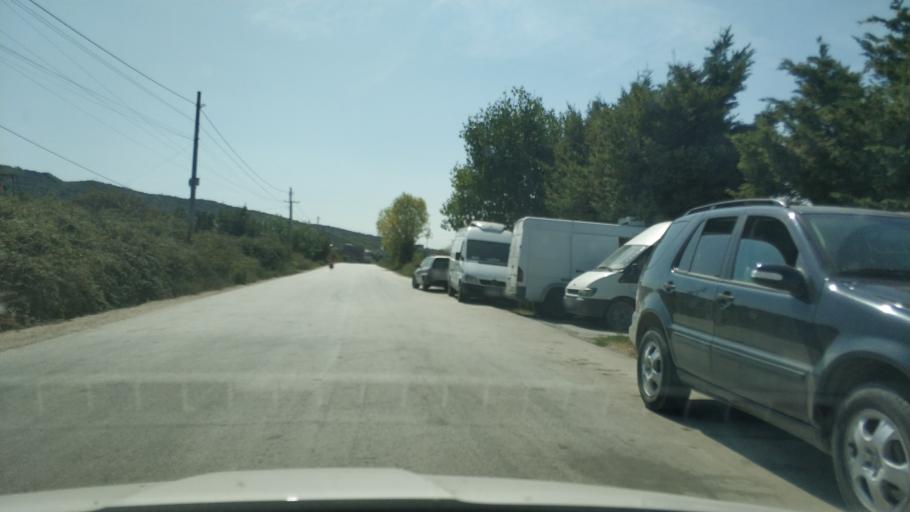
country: AL
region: Fier
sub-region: Rrethi i Lushnjes
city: Grabjan
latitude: 40.9453
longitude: 19.5371
